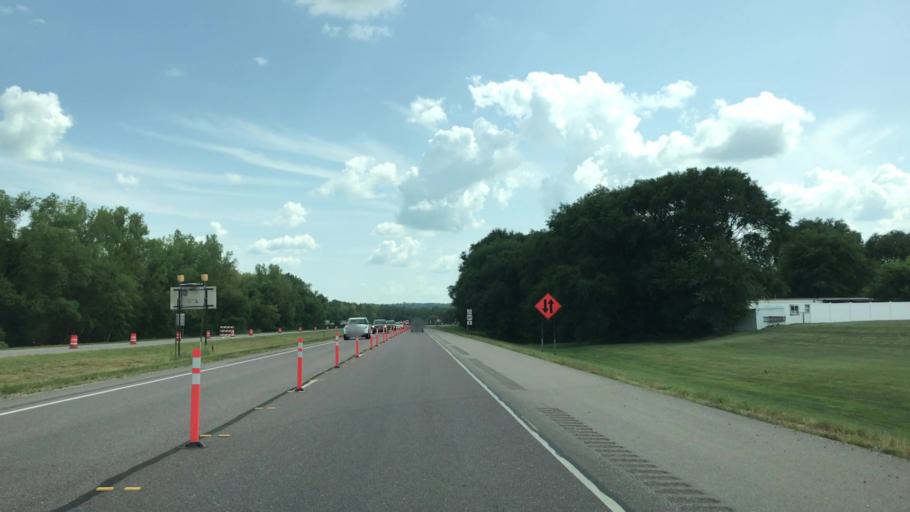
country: US
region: Minnesota
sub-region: Nicollet County
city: Saint Peter
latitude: 44.3458
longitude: -93.9506
